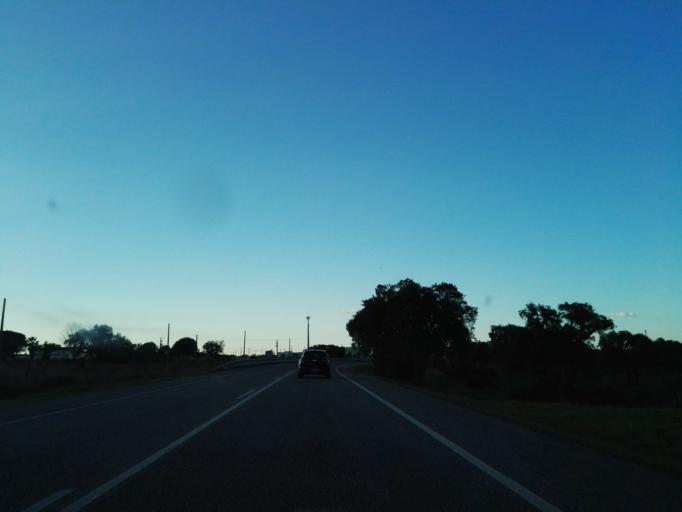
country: PT
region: Santarem
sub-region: Benavente
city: Samora Correia
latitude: 38.8964
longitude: -8.8377
